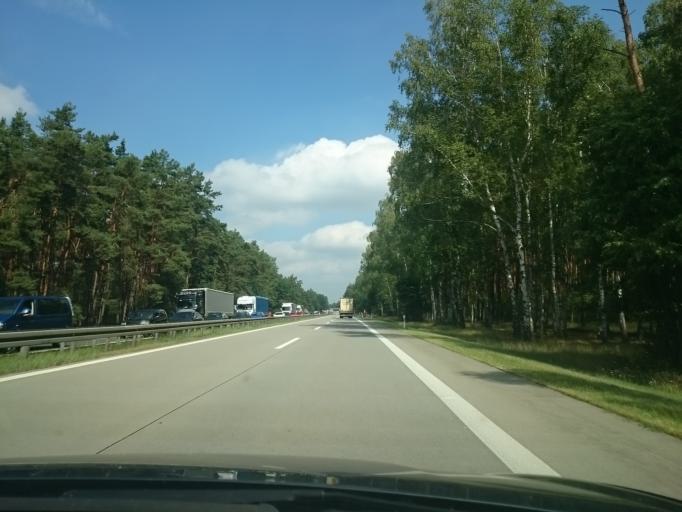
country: DE
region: Brandenburg
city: Marienwerder
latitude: 52.8215
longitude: 13.6478
